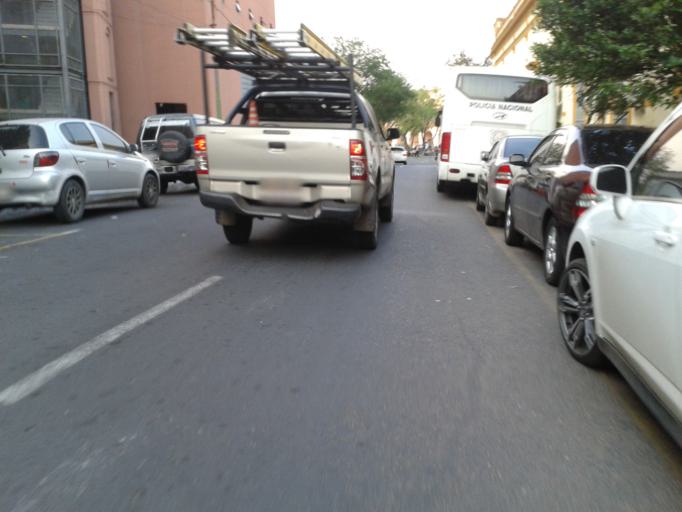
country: PY
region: Asuncion
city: Asuncion
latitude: -25.2814
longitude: -57.6346
